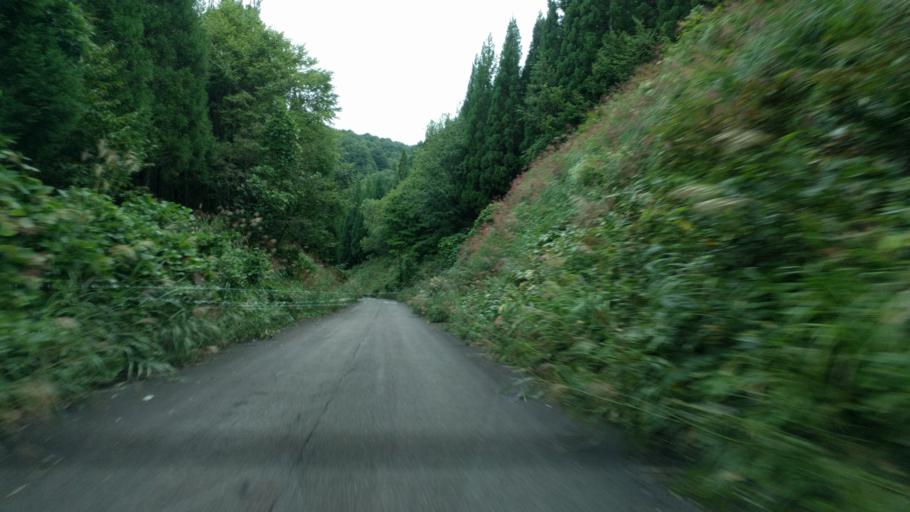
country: JP
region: Fukushima
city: Kitakata
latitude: 37.4632
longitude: 139.7822
